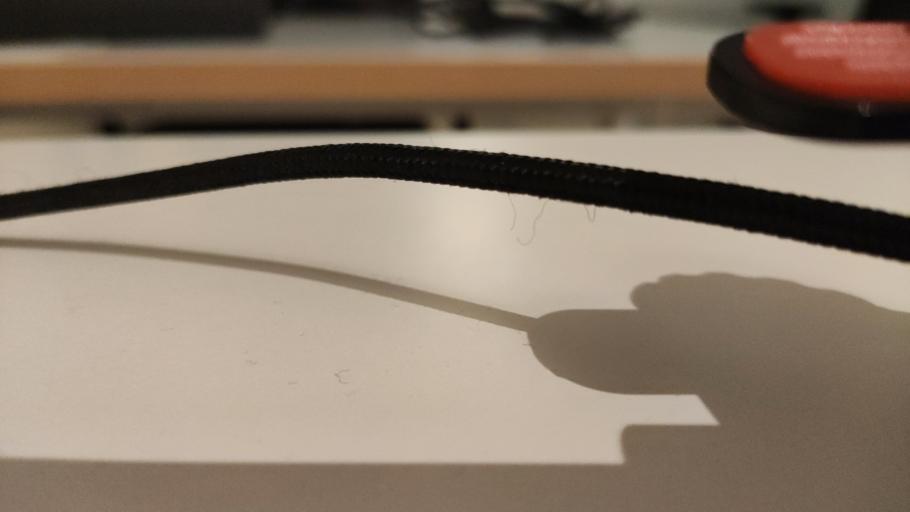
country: RU
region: Moskovskaya
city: Malaya Dubna
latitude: 55.8504
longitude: 38.9637
